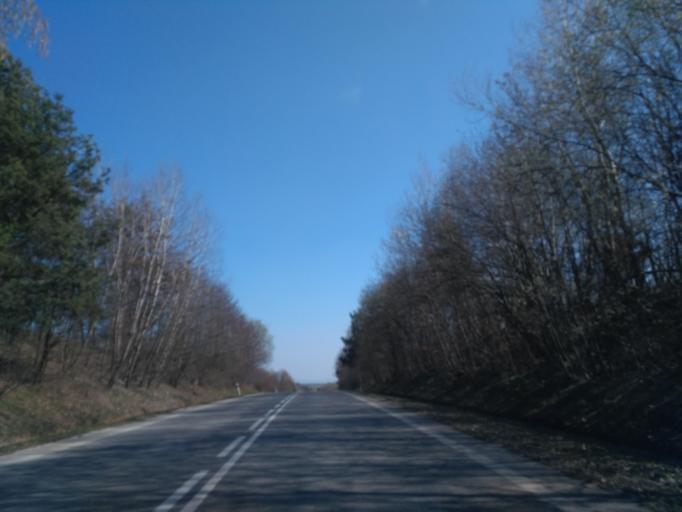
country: SK
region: Kosicky
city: Moldava nad Bodvou
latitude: 48.6895
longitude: 21.0578
